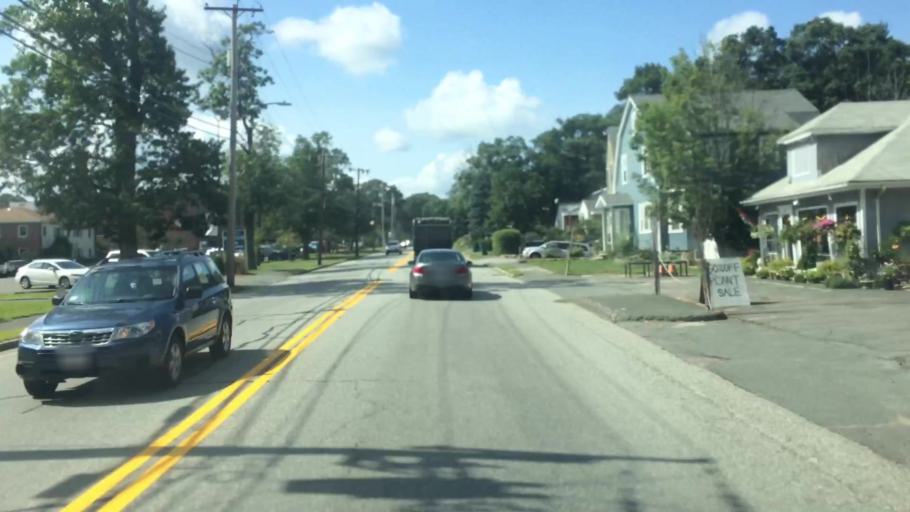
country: US
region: Massachusetts
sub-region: Essex County
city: South Peabody
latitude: 42.5011
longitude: -70.9775
